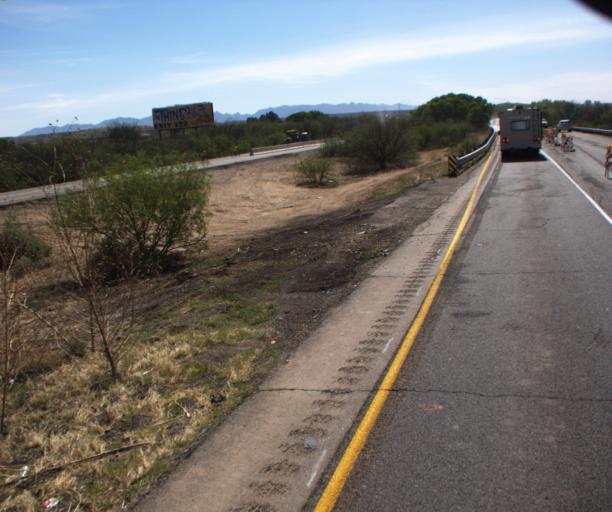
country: US
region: Arizona
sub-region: Cochise County
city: Benson
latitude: 31.9695
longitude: -110.2811
